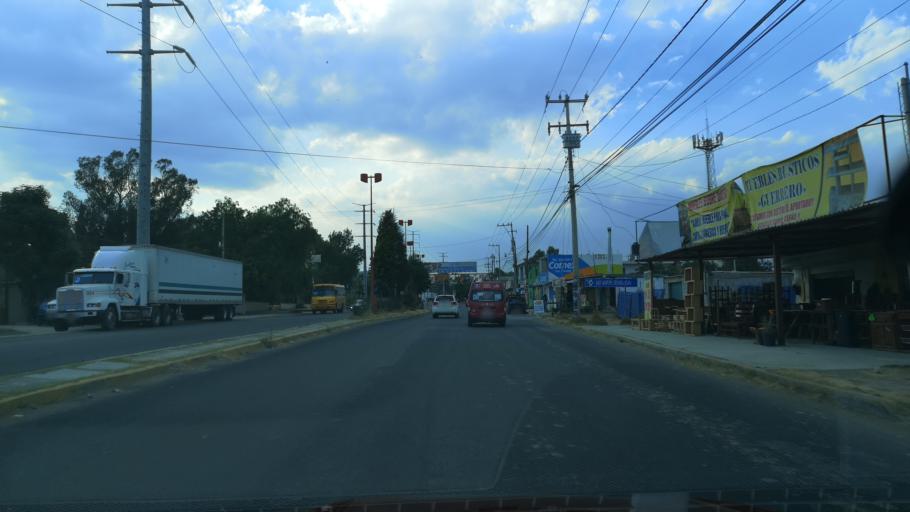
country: MX
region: Puebla
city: Cuanala
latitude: 19.0967
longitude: -98.3419
